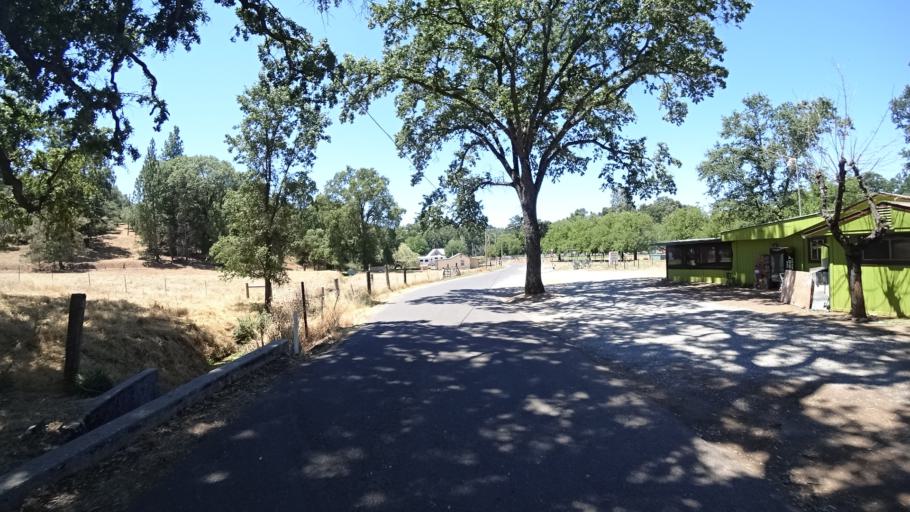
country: US
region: California
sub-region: Calaveras County
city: Mountain Ranch
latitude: 38.2274
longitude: -120.5426
